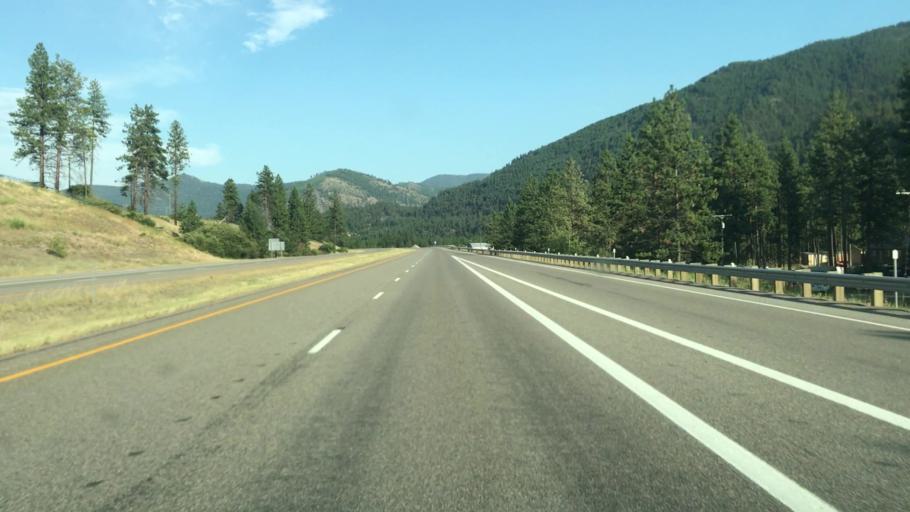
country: US
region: Montana
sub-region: Missoula County
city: Frenchtown
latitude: 47.0042
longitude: -114.4911
